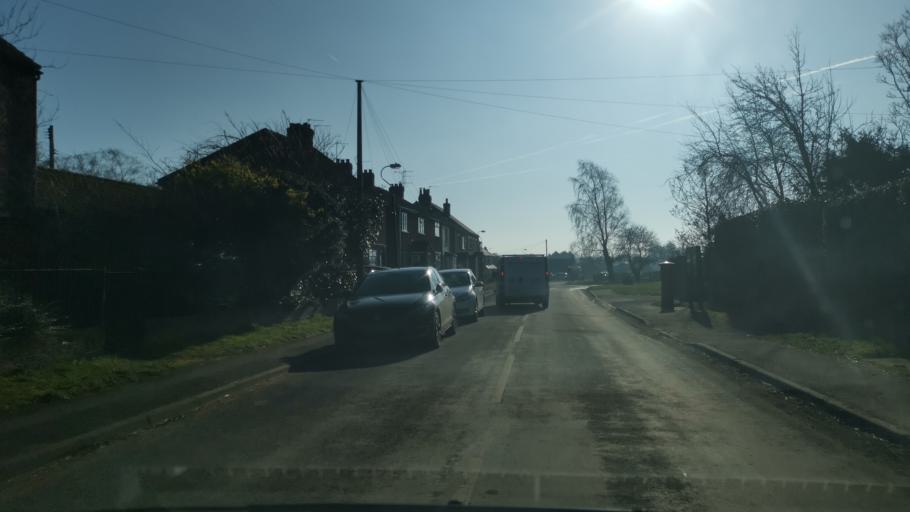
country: GB
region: England
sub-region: City of York
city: Murton
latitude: 53.9667
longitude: -1.0111
